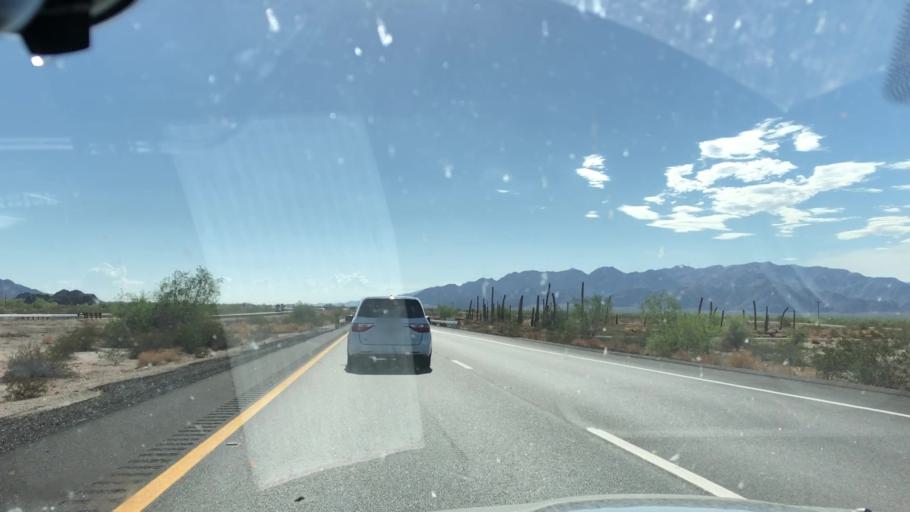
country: US
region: California
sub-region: Imperial County
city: Niland
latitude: 33.7106
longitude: -115.4055
